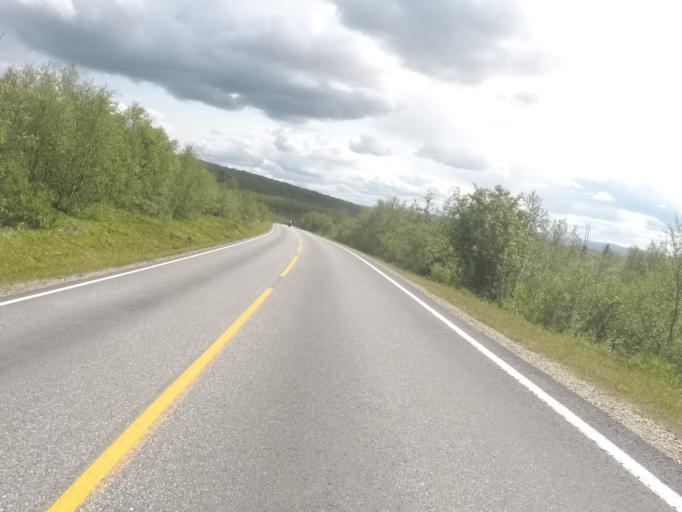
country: NO
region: Finnmark Fylke
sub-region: Karasjok
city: Karasjohka
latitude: 69.5123
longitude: 25.4659
